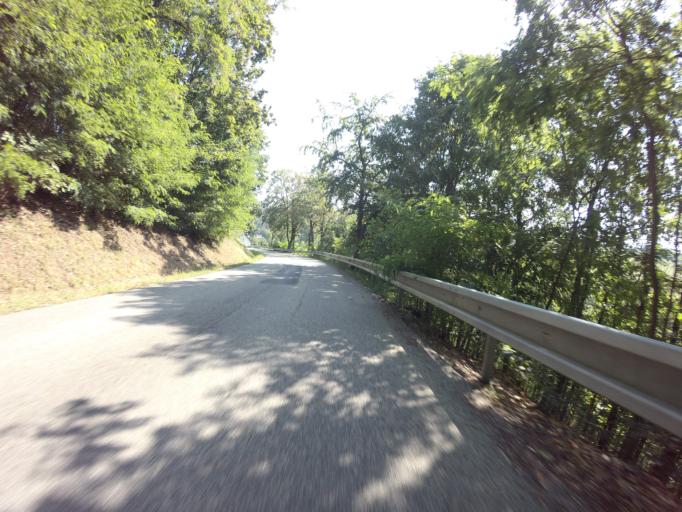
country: CZ
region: Jihocesky
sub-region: Okres Cesky Krumlov
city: Cesky Krumlov
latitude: 48.8524
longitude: 14.3661
